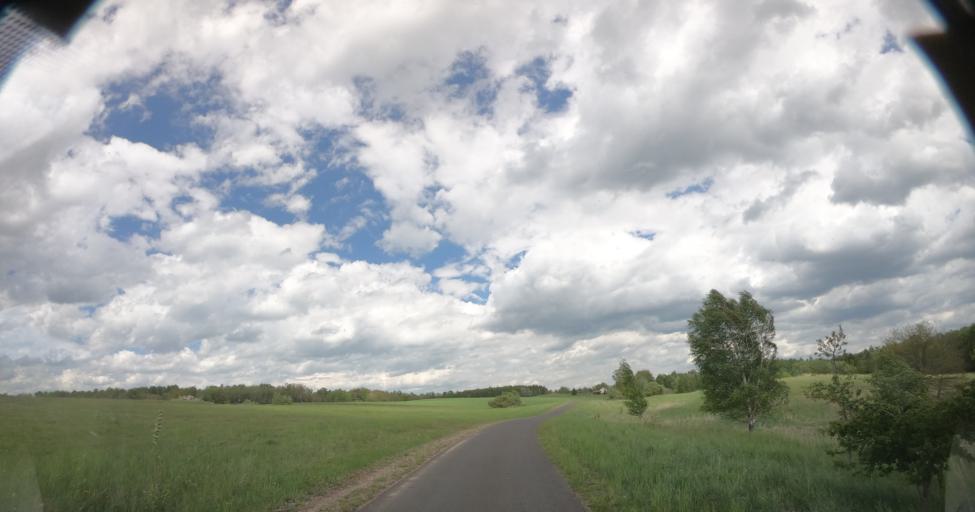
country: PL
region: West Pomeranian Voivodeship
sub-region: Powiat drawski
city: Drawsko Pomorskie
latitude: 53.5617
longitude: 15.7816
